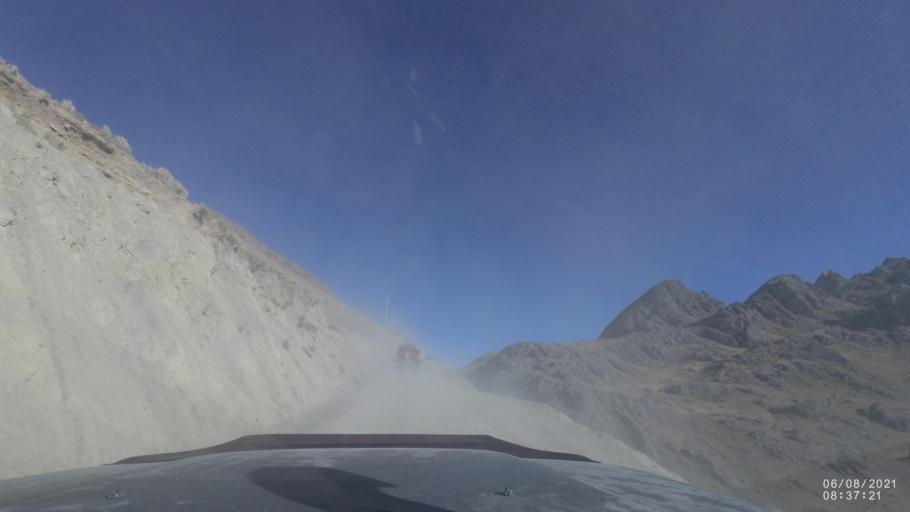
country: BO
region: Cochabamba
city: Sipe Sipe
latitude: -17.1756
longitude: -66.3885
